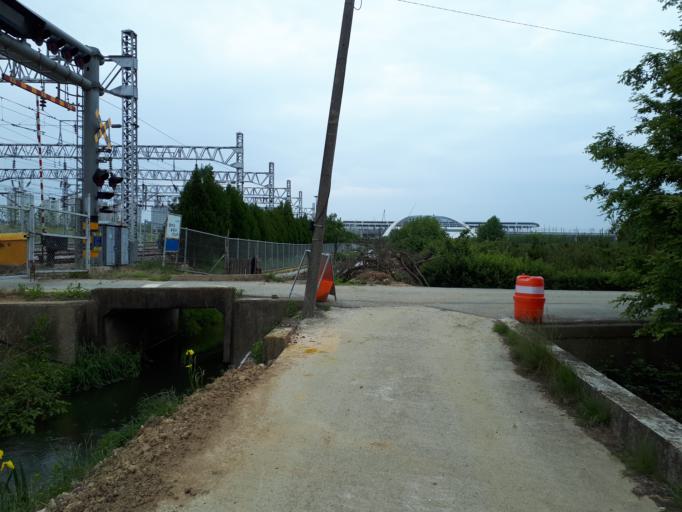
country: KR
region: Chungcheongbuk-do
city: Cheongju-si
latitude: 36.6161
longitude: 127.3212
